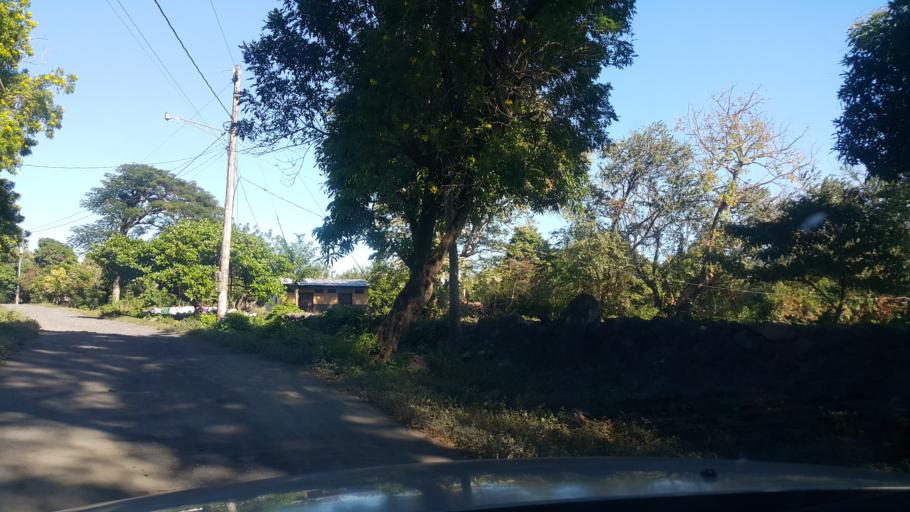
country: NI
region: Rivas
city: Altagracia
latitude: 11.4887
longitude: -85.6087
